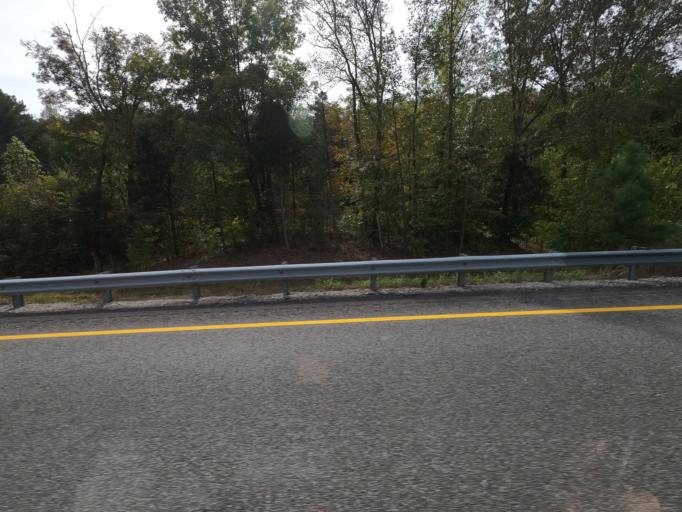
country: US
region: Tennessee
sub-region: Decatur County
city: Parsons
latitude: 35.8149
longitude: -88.2096
